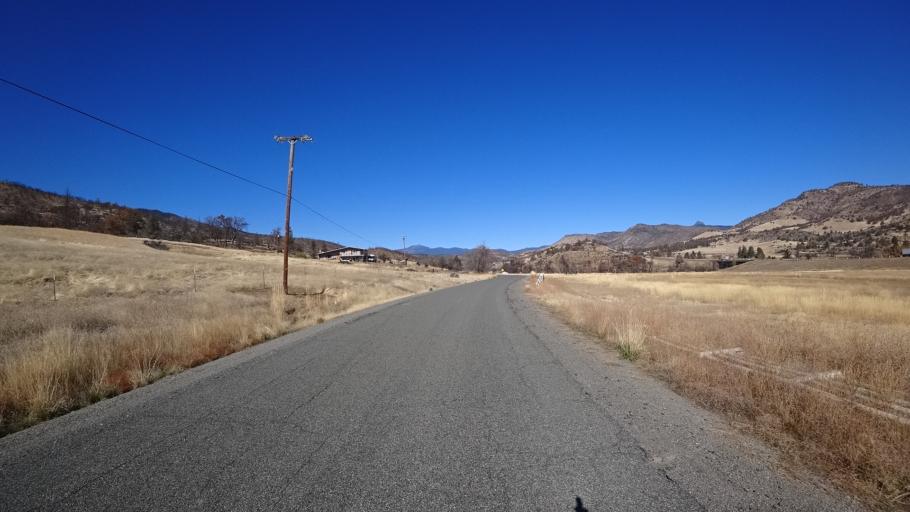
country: US
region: California
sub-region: Siskiyou County
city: Yreka
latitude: 41.9275
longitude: -122.5833
